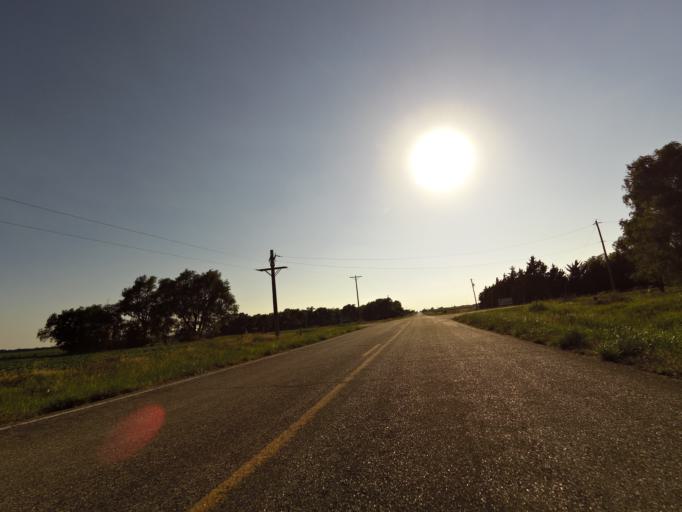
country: US
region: Kansas
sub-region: McPherson County
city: Moundridge
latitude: 38.1451
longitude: -97.5914
